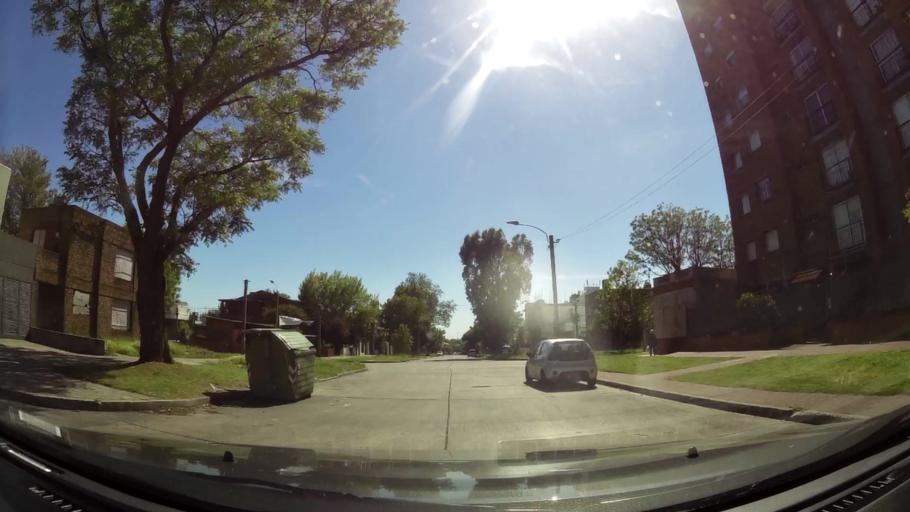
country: UY
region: Montevideo
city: Montevideo
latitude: -34.8878
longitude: -56.1396
